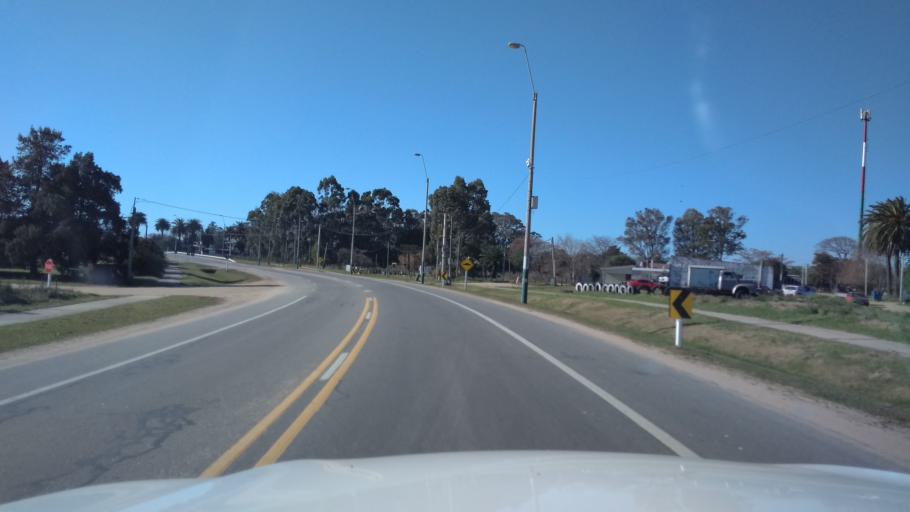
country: UY
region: Canelones
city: Atlantida
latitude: -34.7427
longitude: -55.7660
